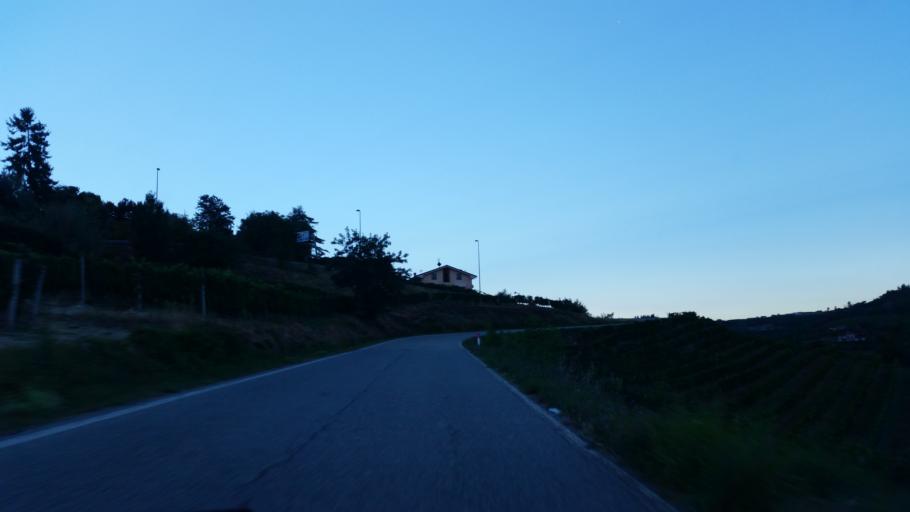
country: IT
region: Piedmont
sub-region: Provincia di Cuneo
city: Mango
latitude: 44.6898
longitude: 8.1452
